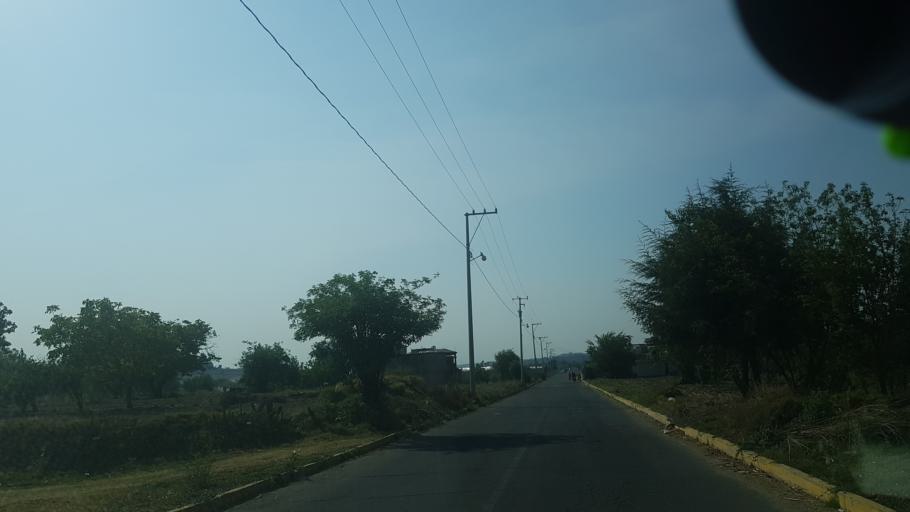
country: MX
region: Puebla
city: San Nicolas de los Ranchos
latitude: 19.0689
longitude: -98.4752
